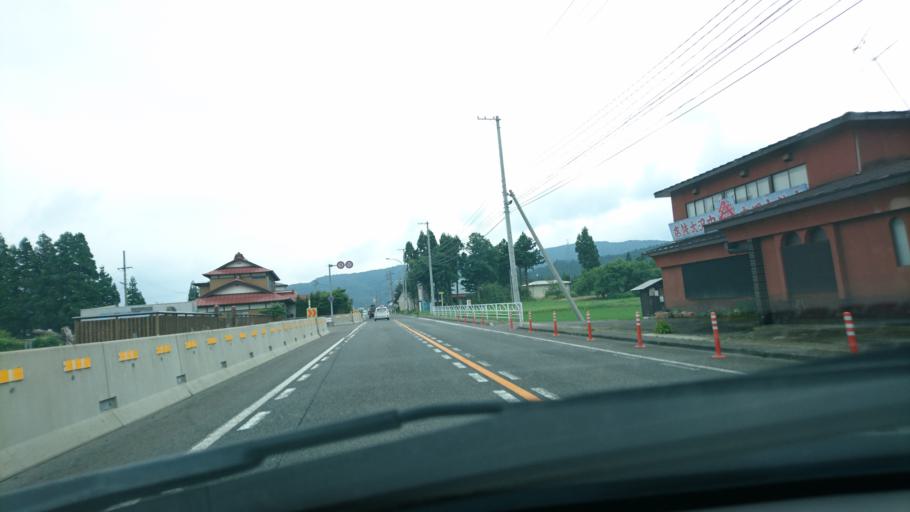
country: JP
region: Miyagi
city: Furukawa
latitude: 38.7365
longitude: 140.7478
